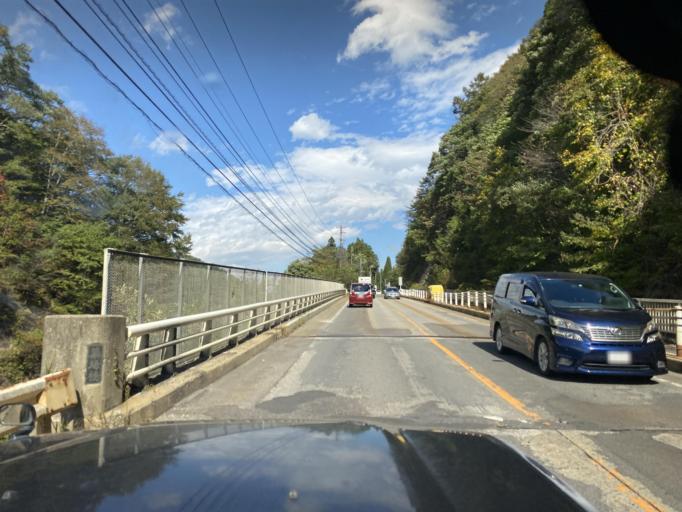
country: JP
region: Nagano
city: Omachi
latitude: 36.5905
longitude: 137.8428
